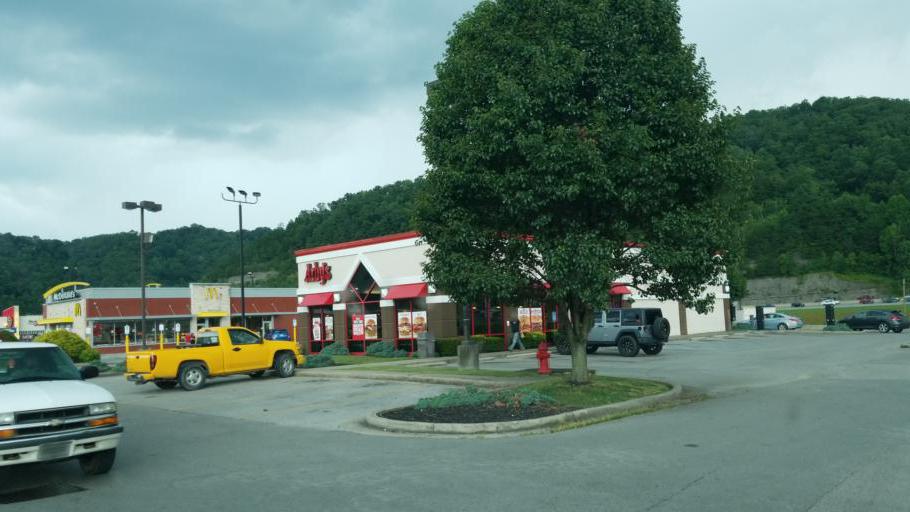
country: US
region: Kentucky
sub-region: Pike County
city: Coal Run Village
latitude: 37.5042
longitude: -82.5351
